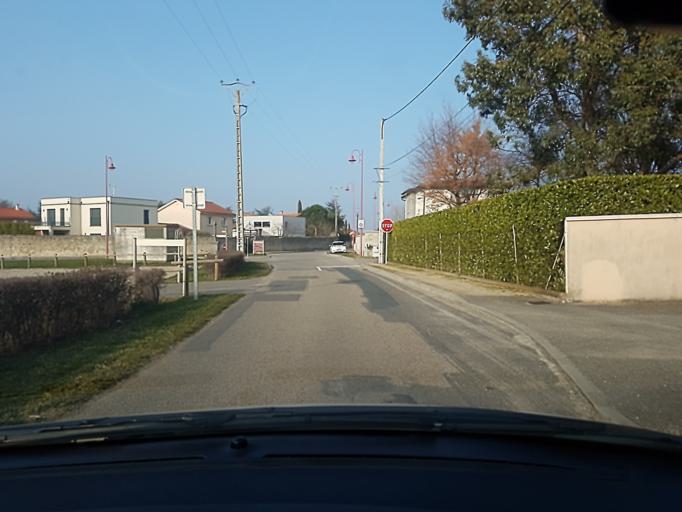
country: FR
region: Rhone-Alpes
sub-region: Departement du Rhone
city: Taluyers
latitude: 45.6362
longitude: 4.7193
